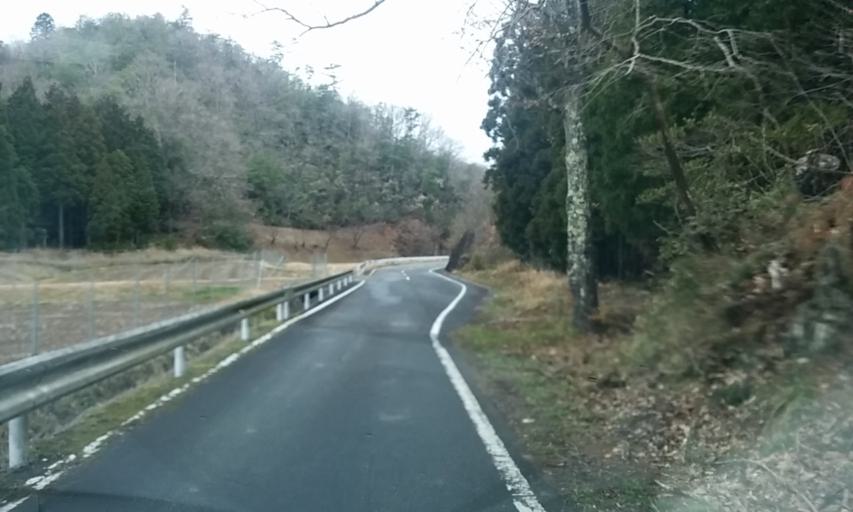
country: JP
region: Kyoto
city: Kameoka
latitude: 35.1163
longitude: 135.4222
